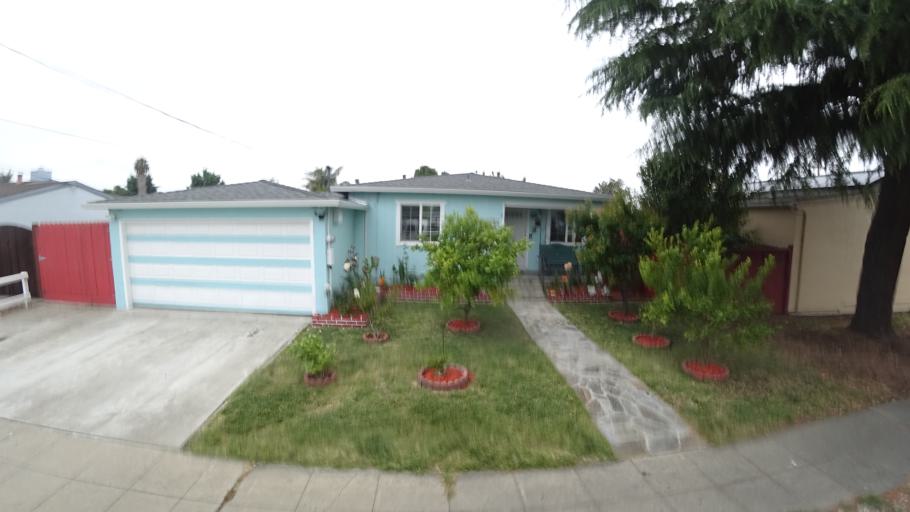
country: US
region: California
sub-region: Alameda County
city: Hayward
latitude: 37.6377
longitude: -122.0814
